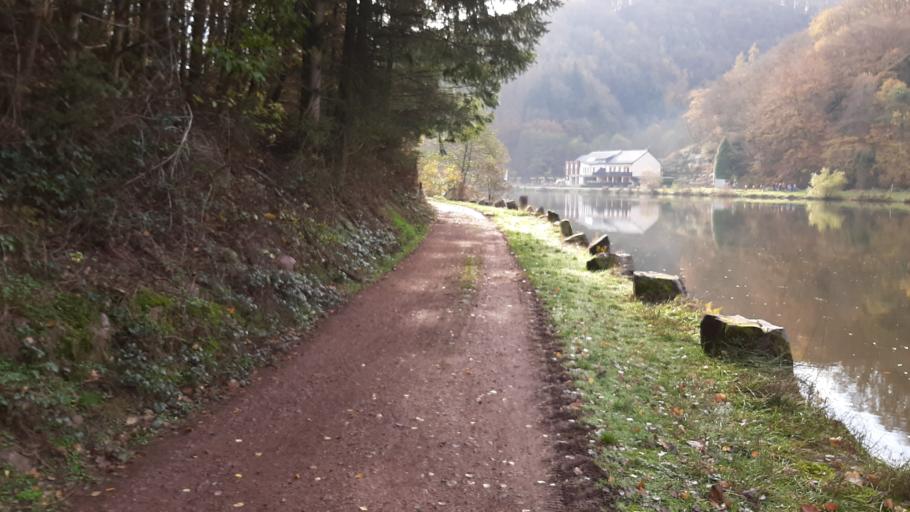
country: DE
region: Saarland
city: Orscholz
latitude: 49.4996
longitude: 6.5451
